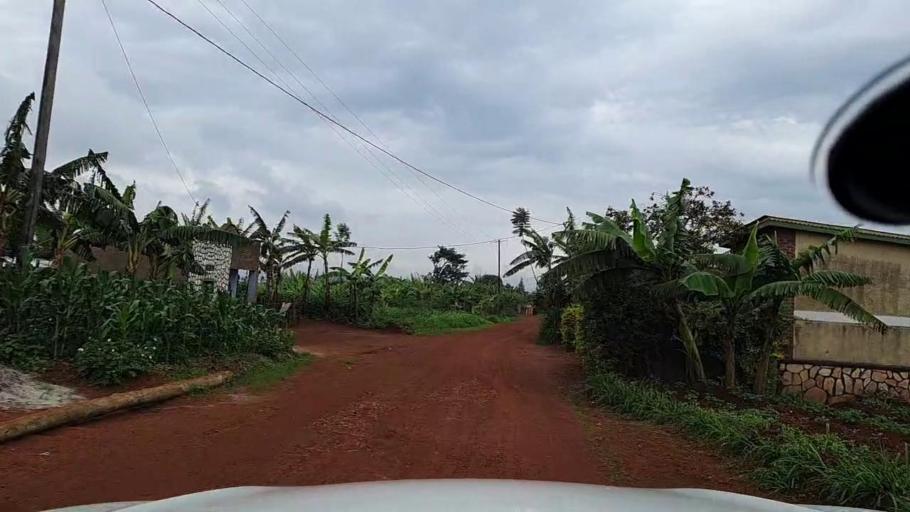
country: RW
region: Kigali
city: Kigali
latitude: -1.9257
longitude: 29.8995
